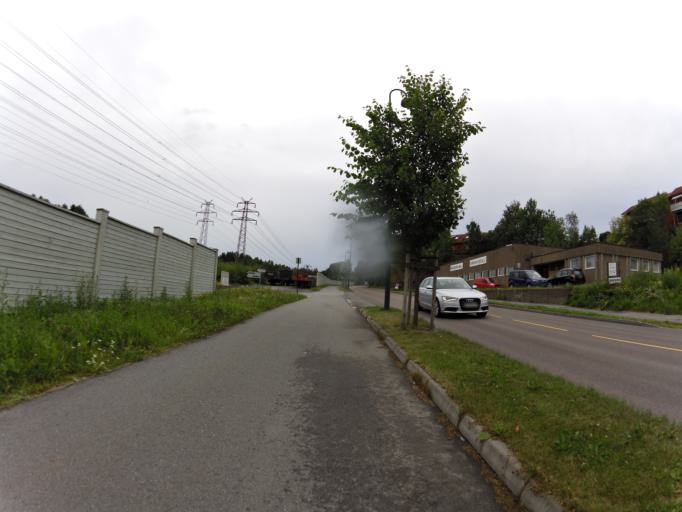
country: NO
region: Ostfold
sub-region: Moss
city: Moss
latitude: 59.4500
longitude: 10.6878
